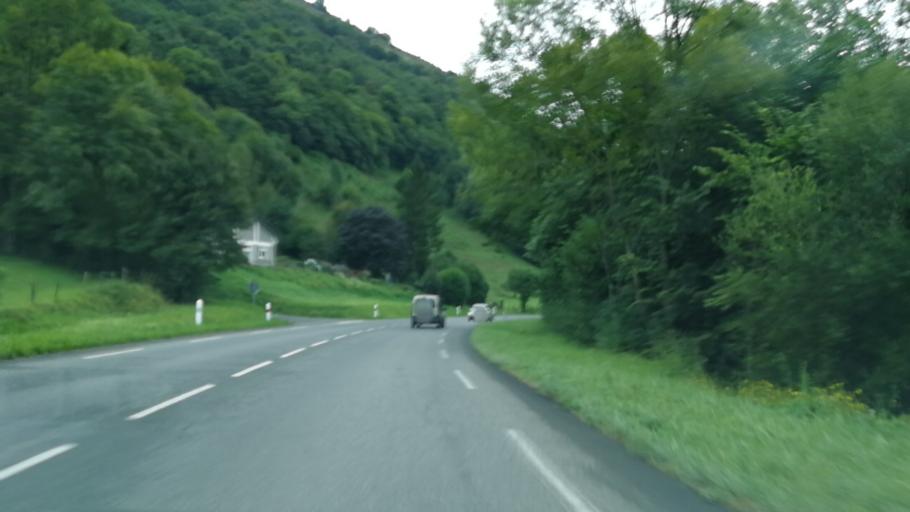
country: FR
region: Aquitaine
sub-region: Departement des Pyrenees-Atlantiques
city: Arette
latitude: 43.0960
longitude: -0.6220
